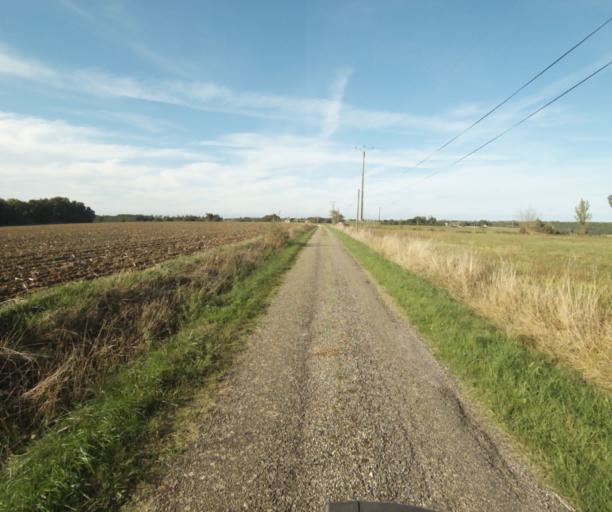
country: FR
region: Midi-Pyrenees
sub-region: Departement du Tarn-et-Garonne
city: Finhan
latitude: 43.9221
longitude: 1.1258
